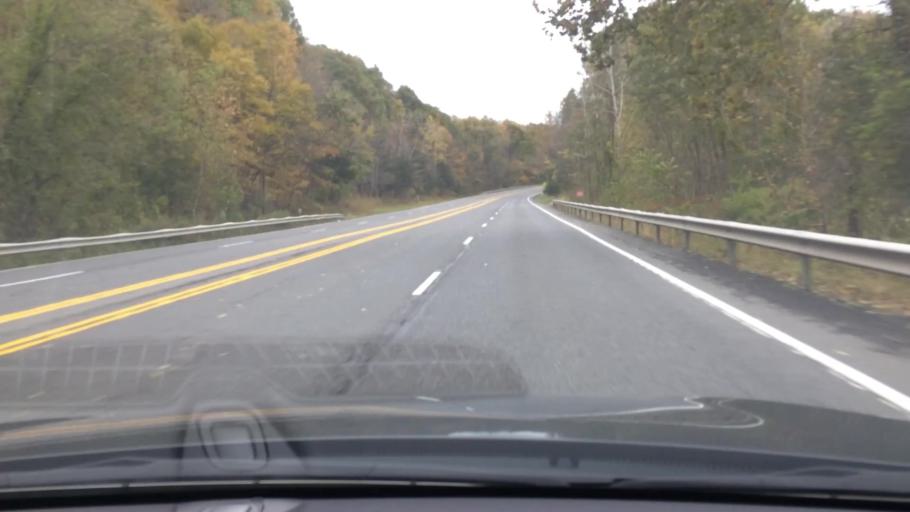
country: US
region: New York
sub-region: Columbia County
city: Kinderhook
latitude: 42.4006
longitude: -73.6878
